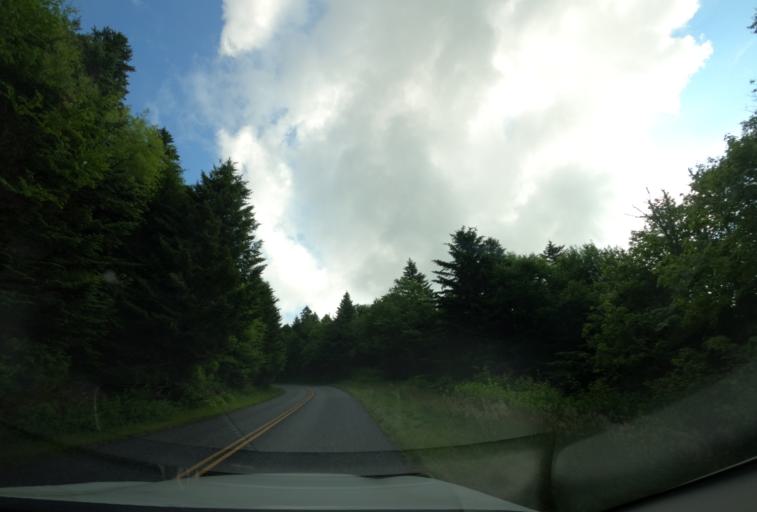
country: US
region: North Carolina
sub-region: Haywood County
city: Hazelwood
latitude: 35.3498
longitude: -82.9742
